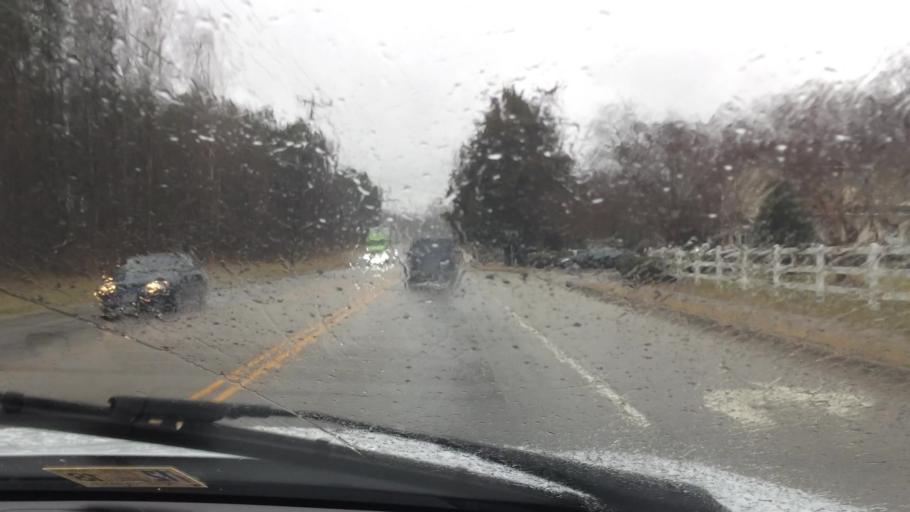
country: US
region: Virginia
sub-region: City of Williamsburg
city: Williamsburg
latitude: 37.2123
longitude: -76.6184
